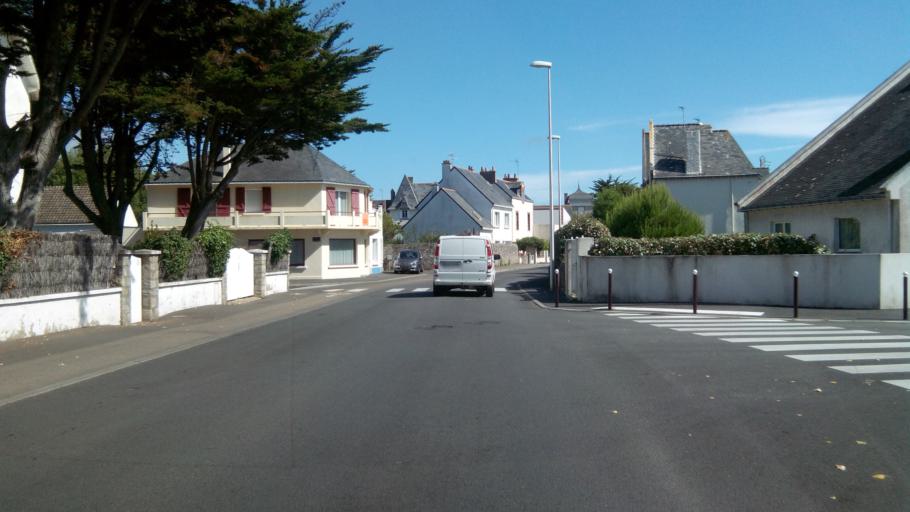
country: FR
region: Pays de la Loire
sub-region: Departement de la Loire-Atlantique
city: Le Croisic
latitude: 47.2890
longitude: -2.5112
